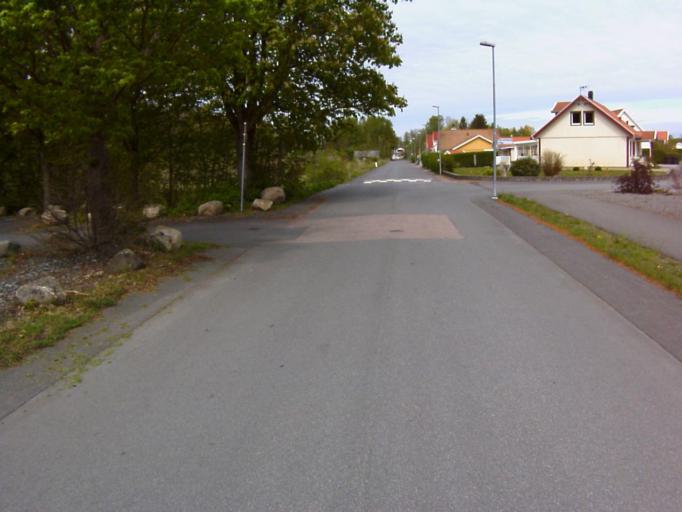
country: SE
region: Skane
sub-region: Kristianstads Kommun
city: Fjalkinge
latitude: 56.0781
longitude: 14.2149
